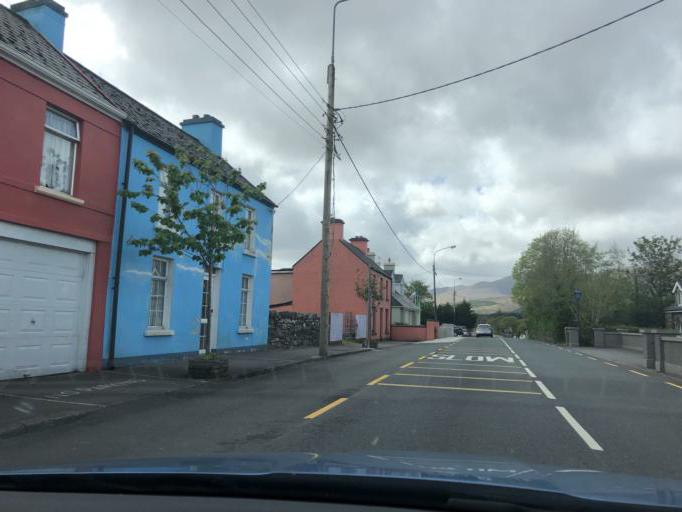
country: IE
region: Munster
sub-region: Ciarrai
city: Killorglin
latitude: 51.8387
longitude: -9.9032
